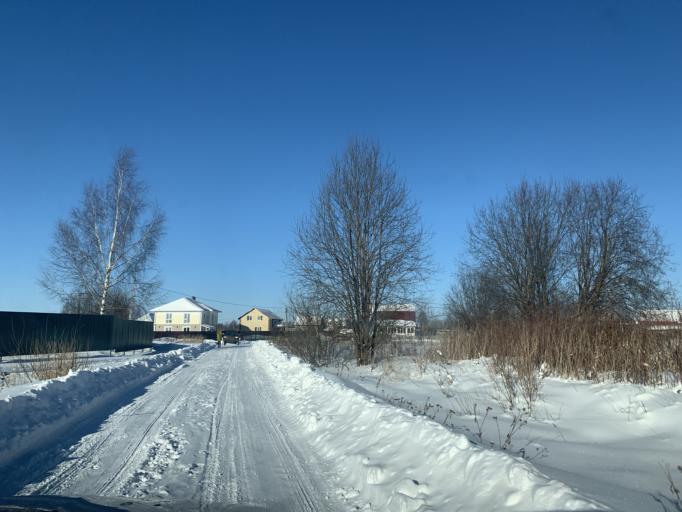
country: RU
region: Jaroslavl
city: Tunoshna
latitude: 57.6622
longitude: 40.0668
